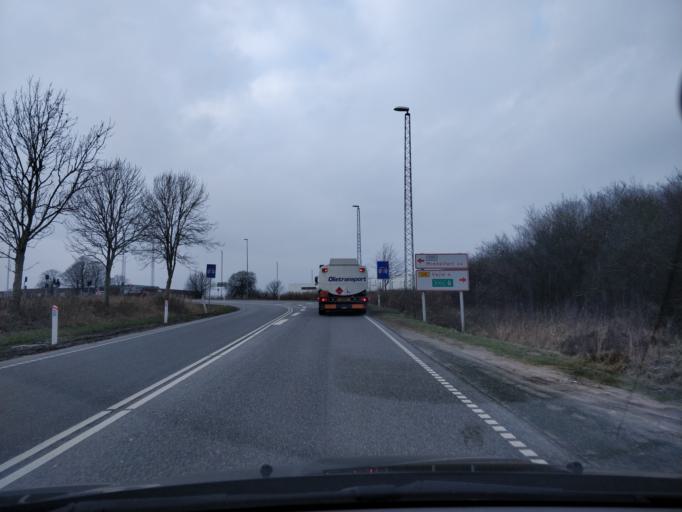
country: DK
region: South Denmark
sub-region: Vejle Kommune
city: Vejle
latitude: 55.6705
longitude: 9.5863
